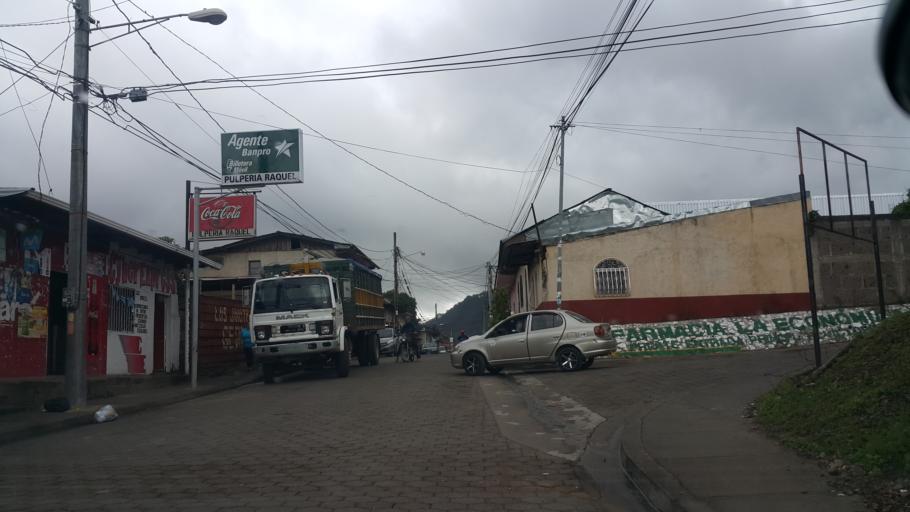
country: NI
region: Jinotega
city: Jinotega
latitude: 13.0860
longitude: -86.0010
